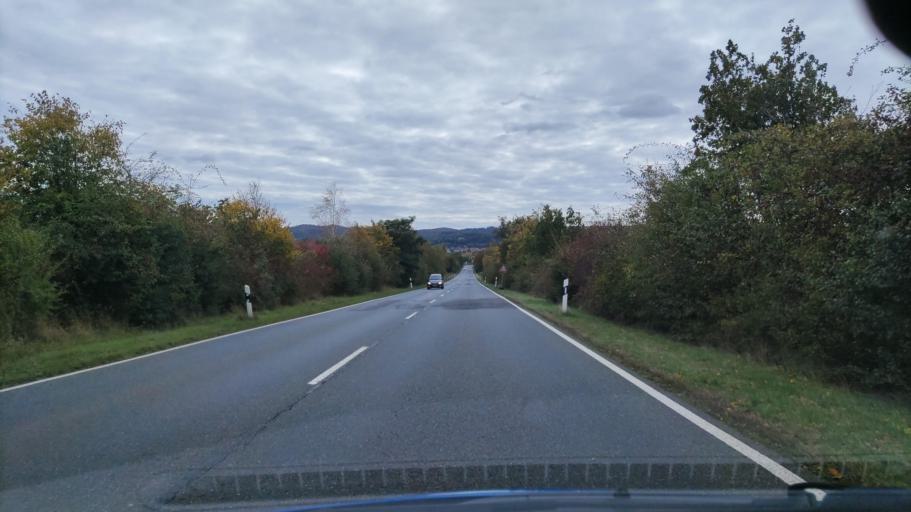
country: DE
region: Saxony-Anhalt
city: Darlingerode
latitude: 51.8552
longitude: 10.7553
